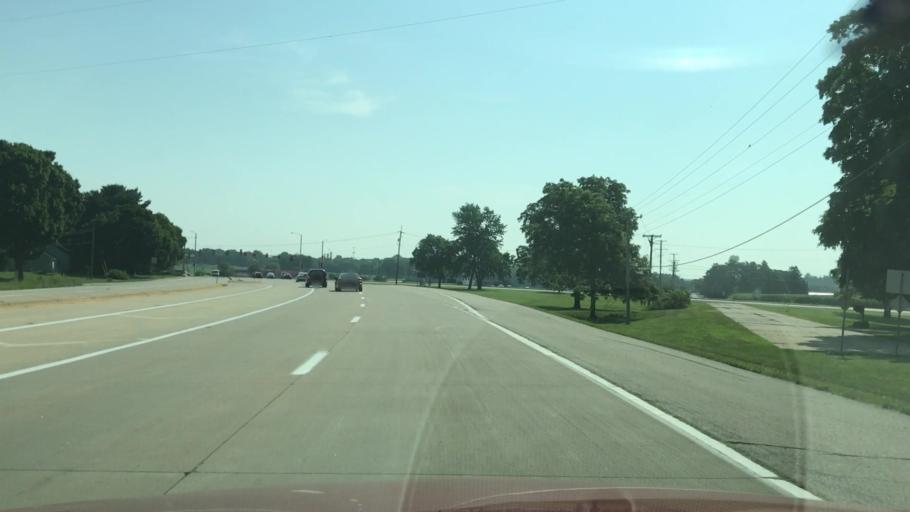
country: US
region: Illinois
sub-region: Winnebago County
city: Cherry Valley
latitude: 42.2388
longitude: -88.9824
